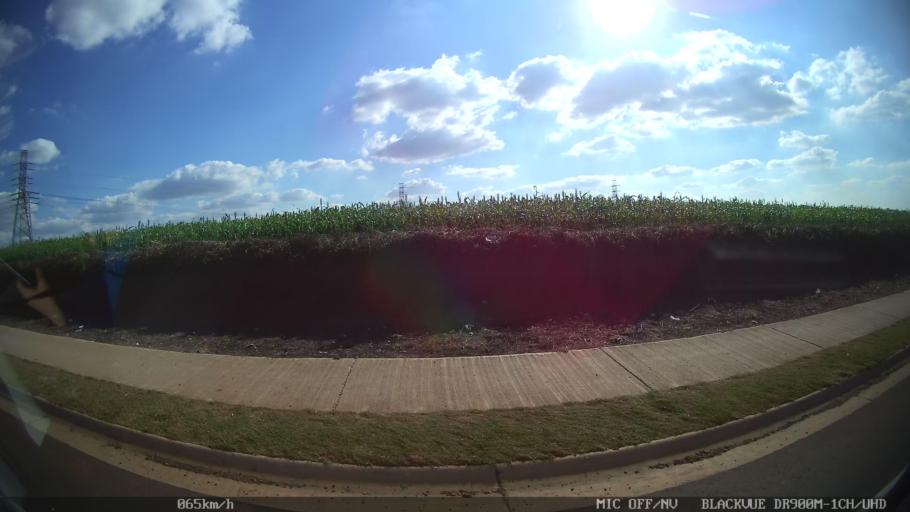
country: BR
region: Sao Paulo
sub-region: Nova Odessa
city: Nova Odessa
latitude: -22.7996
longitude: -47.3167
